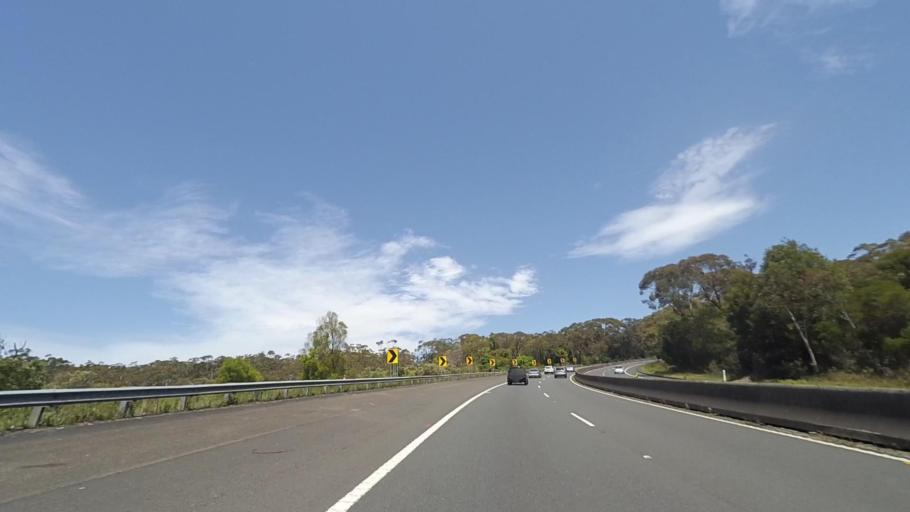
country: AU
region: New South Wales
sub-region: Wollongong
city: Corrimal
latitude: -34.3541
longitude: 150.8640
